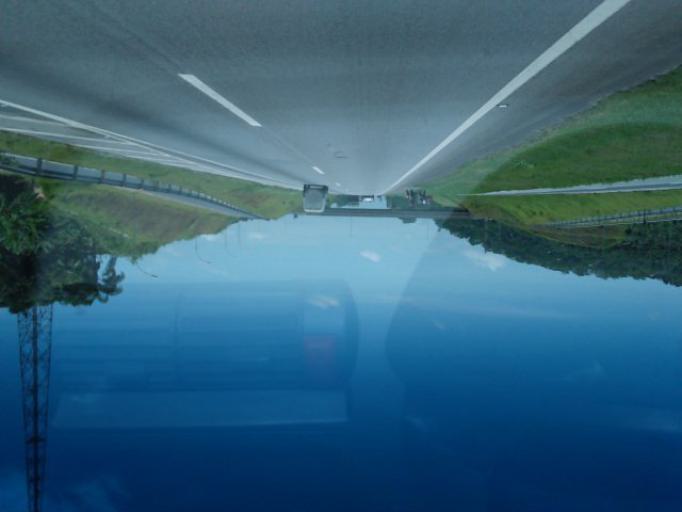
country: BR
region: Sao Paulo
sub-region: Miracatu
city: Miracatu
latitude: -24.3217
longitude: -47.5390
